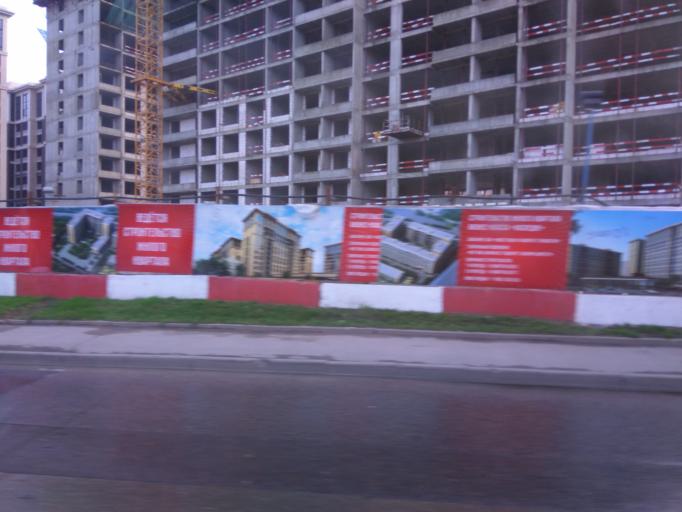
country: RU
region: Moskovskaya
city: Bogorodskoye
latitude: 55.8013
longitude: 37.7113
